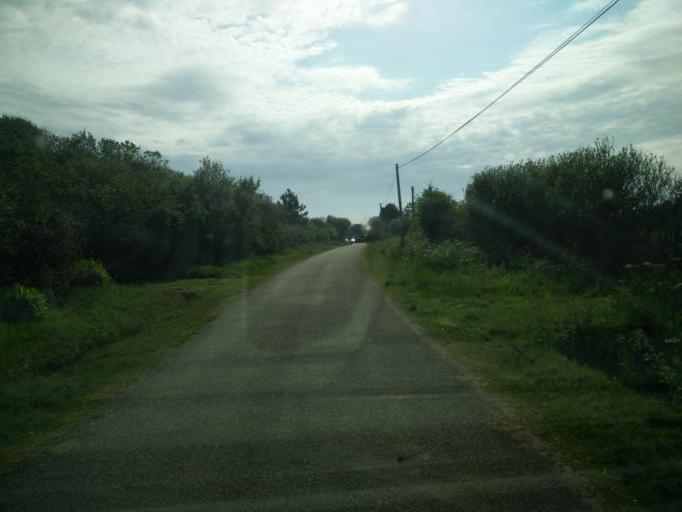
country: FR
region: Brittany
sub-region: Departement du Finistere
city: Camaret-sur-Mer
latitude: 48.2326
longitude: -4.5540
